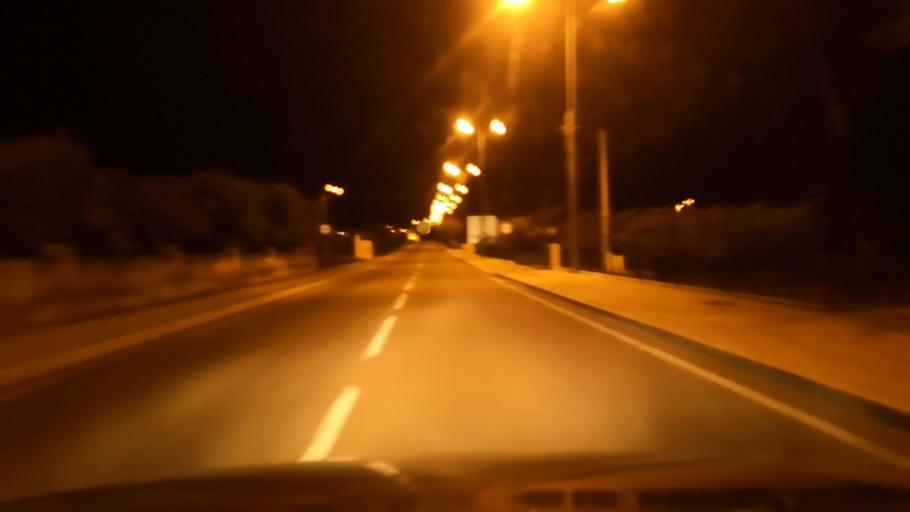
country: PT
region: Evora
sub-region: Estremoz
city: Estremoz
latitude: 38.8457
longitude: -7.5975
